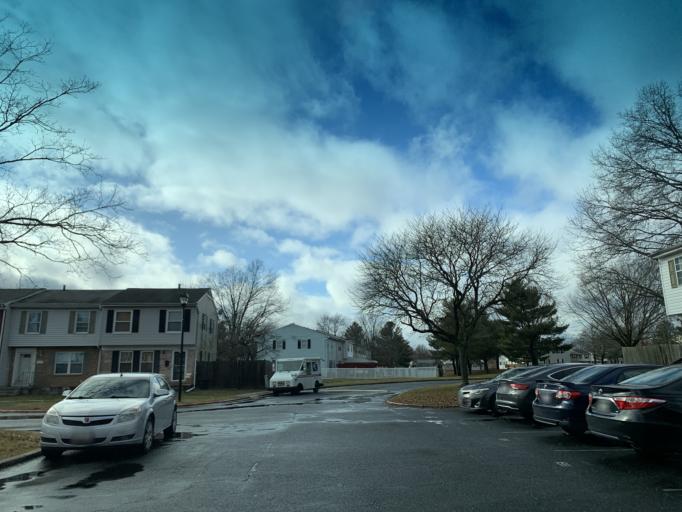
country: US
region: Maryland
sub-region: Harford County
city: Edgewood
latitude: 39.4206
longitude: -76.3155
